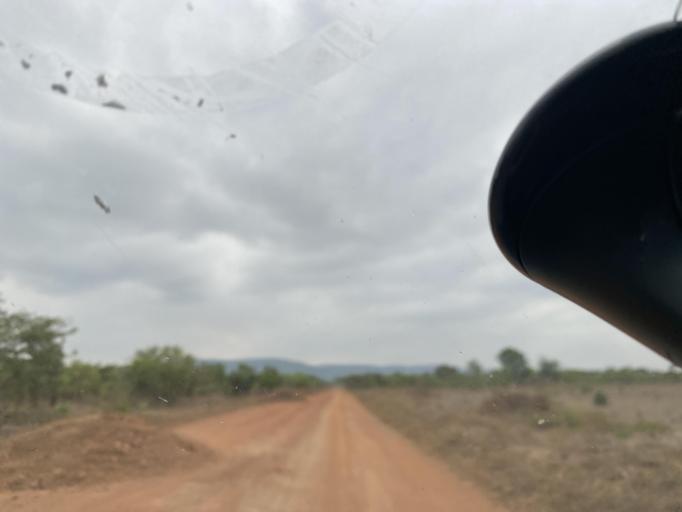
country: ZM
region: Lusaka
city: Chongwe
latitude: -15.2110
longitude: 28.7567
